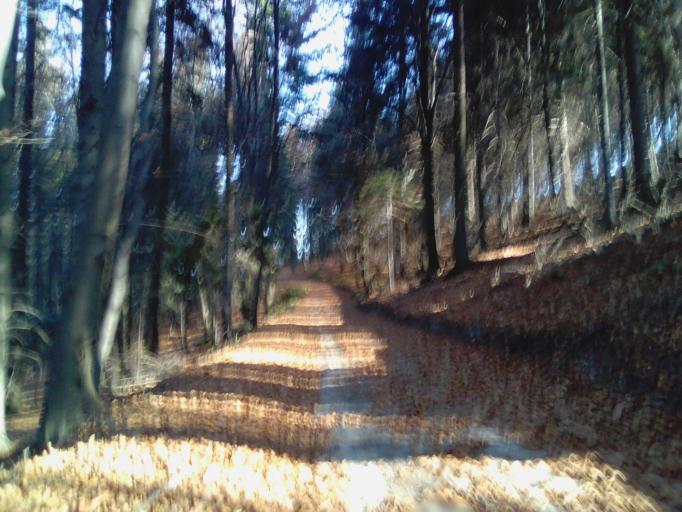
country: PL
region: Subcarpathian Voivodeship
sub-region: Powiat strzyzowski
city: Wysoka Strzyzowska
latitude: 49.8149
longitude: 21.7073
